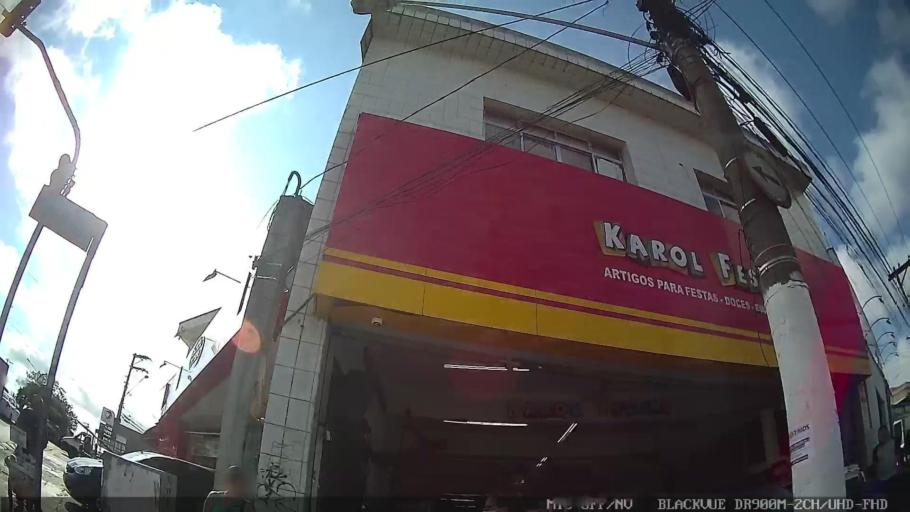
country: BR
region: Sao Paulo
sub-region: Guarulhos
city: Guarulhos
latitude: -23.5433
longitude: -46.4933
